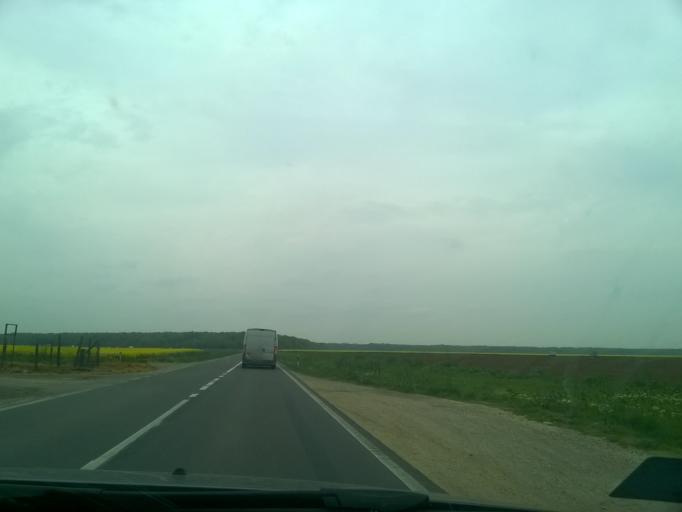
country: RS
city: Hrtkovci
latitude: 44.8489
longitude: 19.7695
